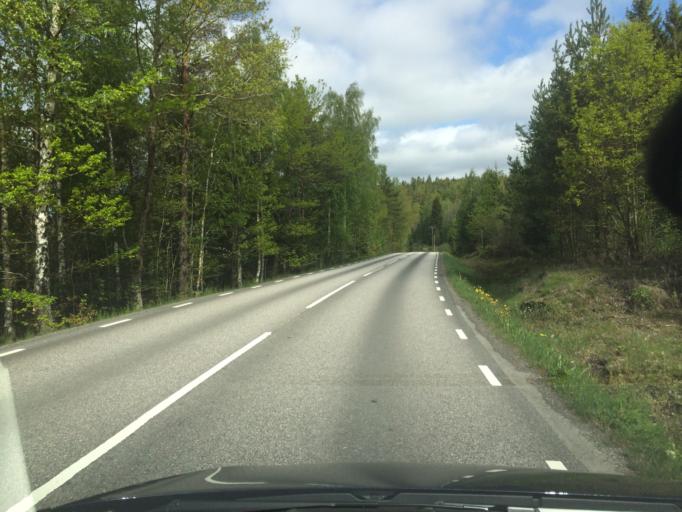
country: SE
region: Vaestra Goetaland
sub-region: Lerums Kommun
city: Stenkullen
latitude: 57.7401
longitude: 12.3393
